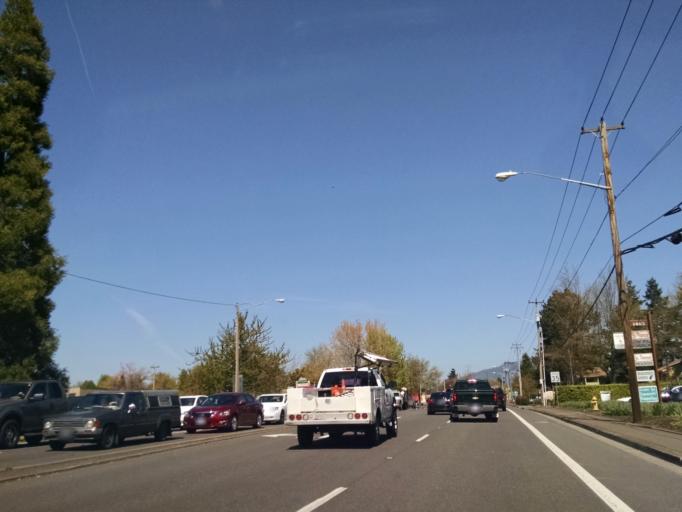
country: US
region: Oregon
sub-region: Lane County
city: Eugene
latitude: 44.0777
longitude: -123.0692
